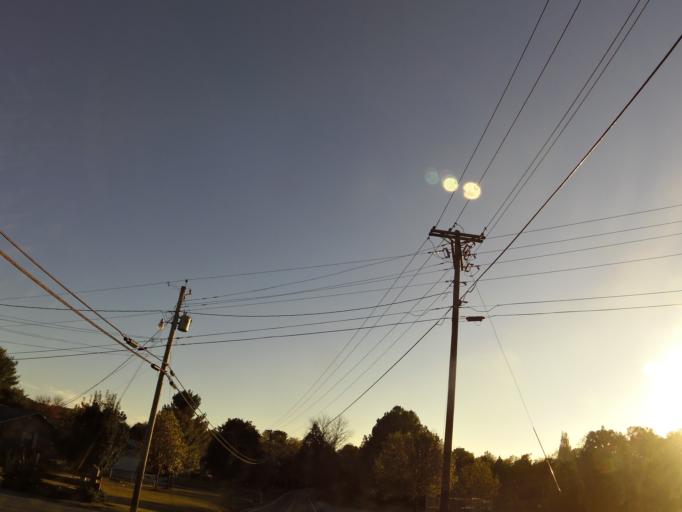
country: US
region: Tennessee
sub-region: Anderson County
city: Clinton
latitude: 36.0091
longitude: -84.0565
